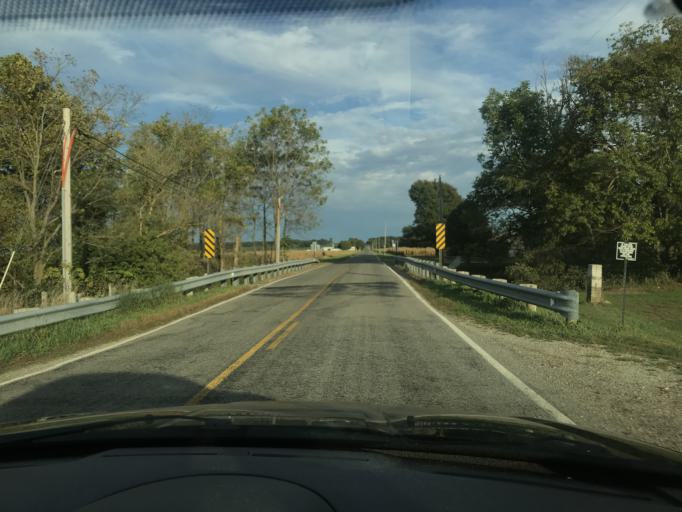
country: US
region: Ohio
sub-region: Logan County
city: West Liberty
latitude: 40.1947
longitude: -83.7971
